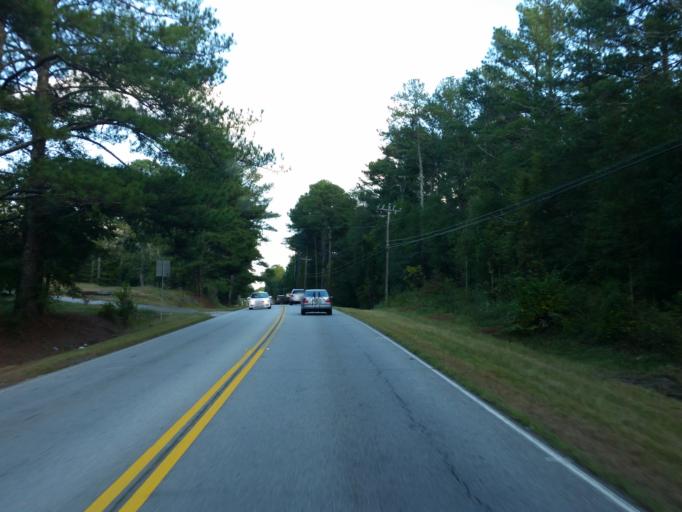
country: US
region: Georgia
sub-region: Paulding County
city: Hiram
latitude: 33.9051
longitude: -84.7326
